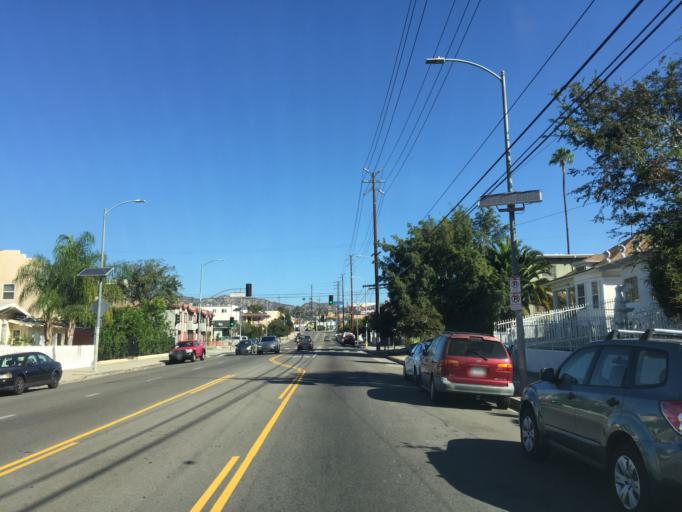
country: US
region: California
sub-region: Los Angeles County
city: Silver Lake
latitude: 34.0927
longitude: -118.2866
